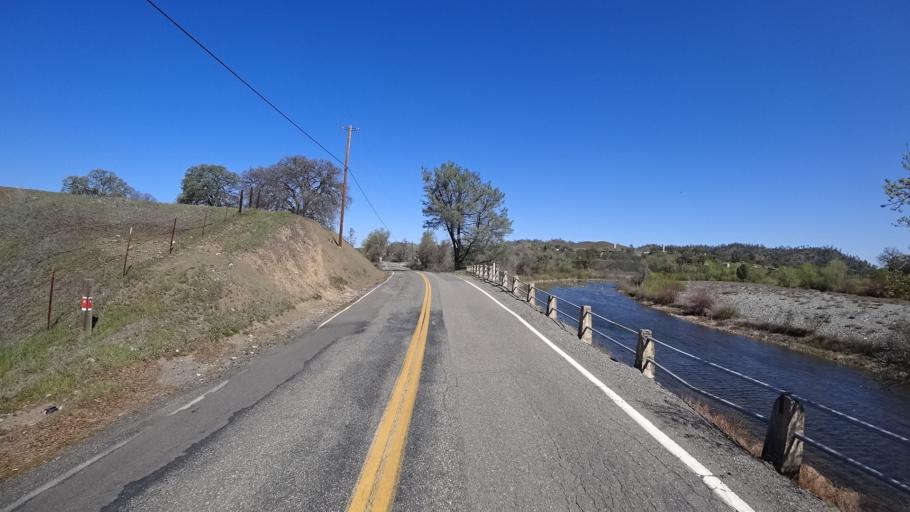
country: US
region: California
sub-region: Glenn County
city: Orland
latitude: 39.6685
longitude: -122.5253
